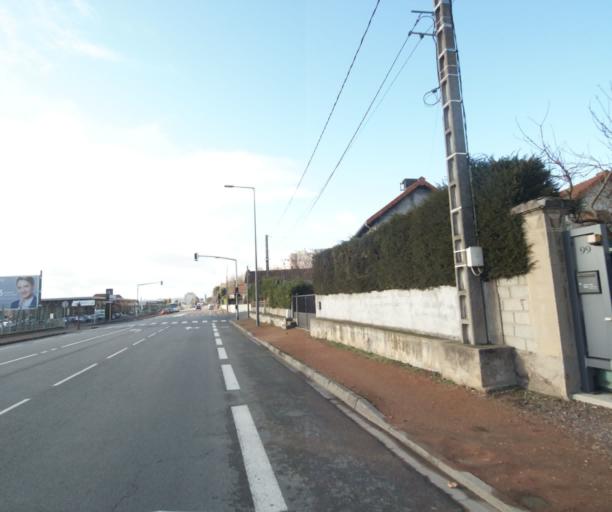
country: FR
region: Rhone-Alpes
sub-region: Departement de la Loire
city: Le Coteau
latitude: 46.0467
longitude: 4.0853
